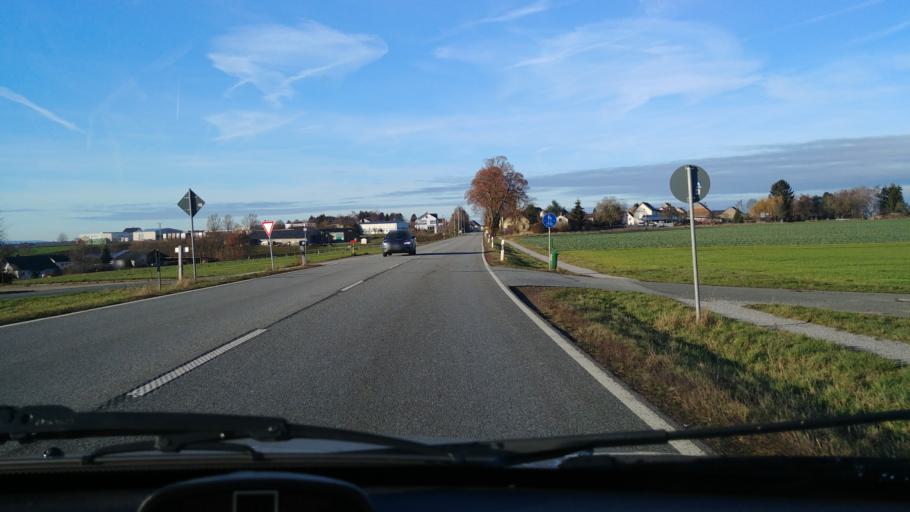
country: DE
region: Rheinland-Pfalz
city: Holzhausen an der Haide
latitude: 50.2129
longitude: 7.9151
